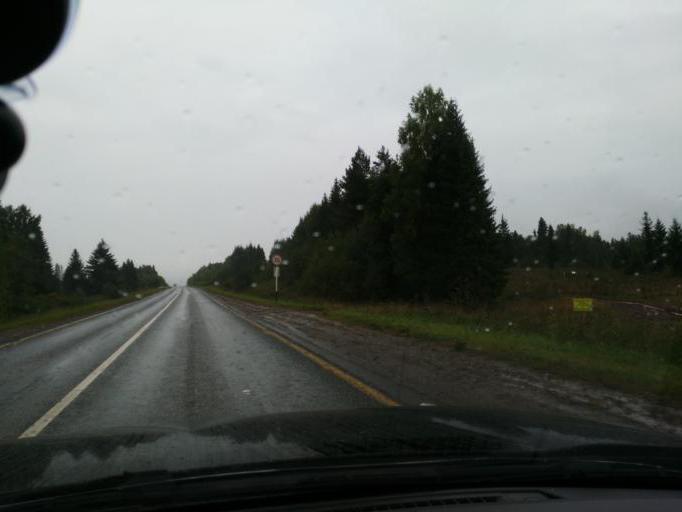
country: RU
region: Perm
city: Yugo-Kamskiy
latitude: 57.5757
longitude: 55.6820
